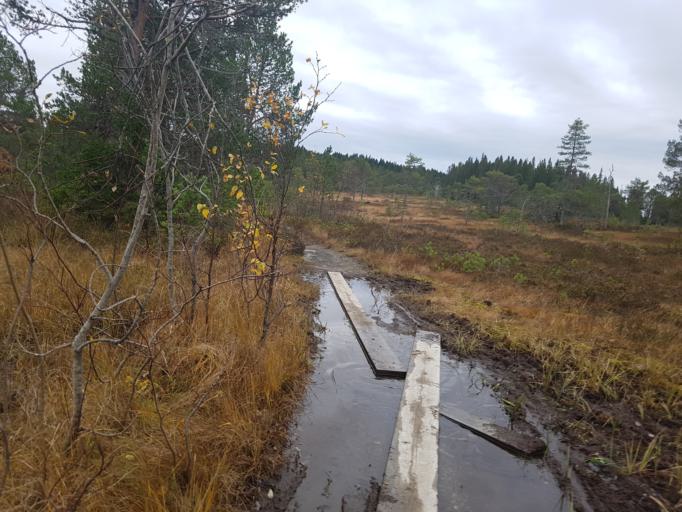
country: NO
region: Sor-Trondelag
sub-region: Melhus
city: Melhus
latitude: 63.3842
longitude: 10.2455
